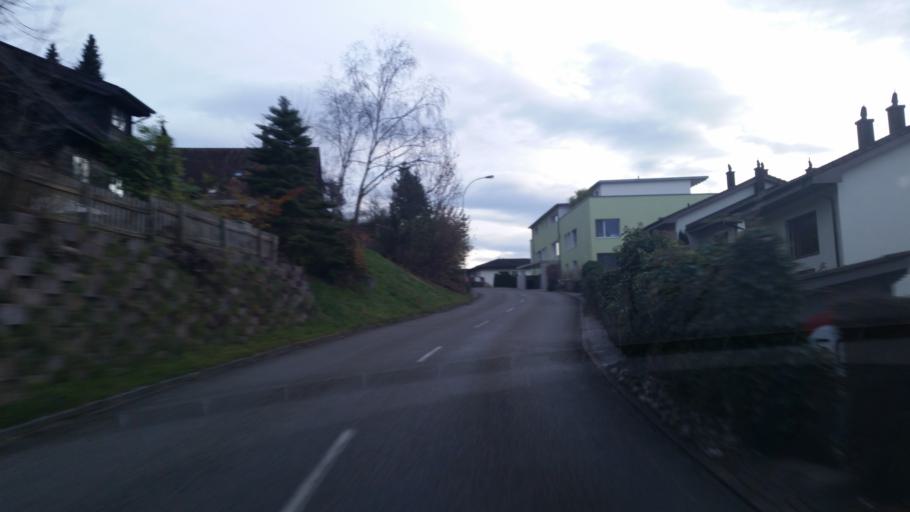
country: CH
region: Aargau
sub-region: Bezirk Baden
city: Kunten
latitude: 47.3889
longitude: 8.3347
